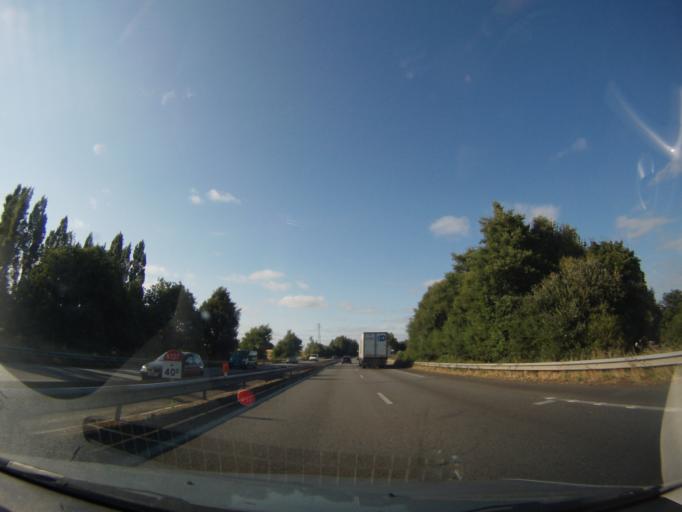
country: FR
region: Pays de la Loire
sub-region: Departement de la Loire-Atlantique
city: Treillieres
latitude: 47.3573
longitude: -1.6562
